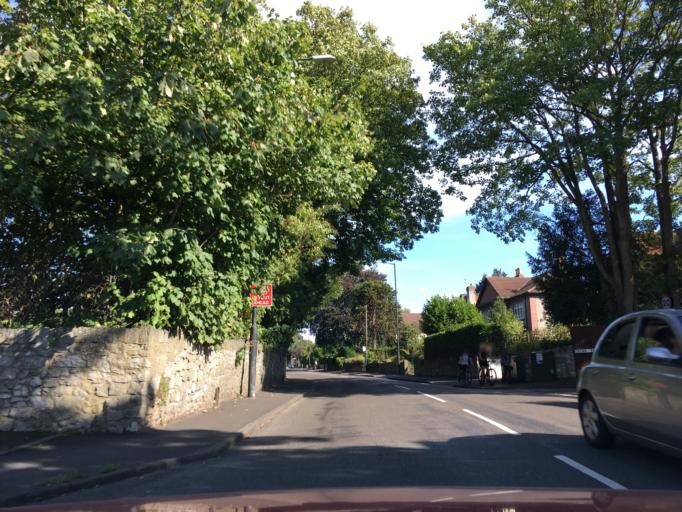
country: GB
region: England
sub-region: Bristol
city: Bristol
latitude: 51.4857
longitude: -2.6394
